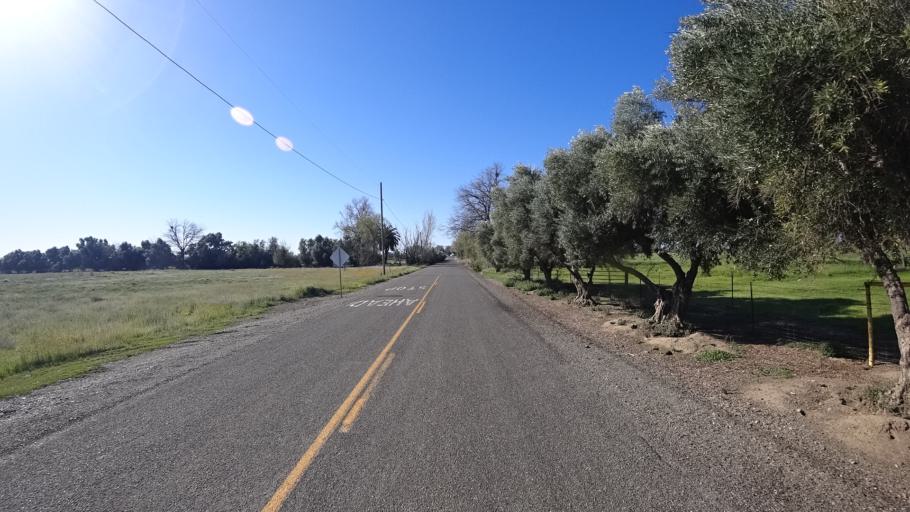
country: US
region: California
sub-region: Glenn County
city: Orland
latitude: 39.7656
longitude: -122.2478
